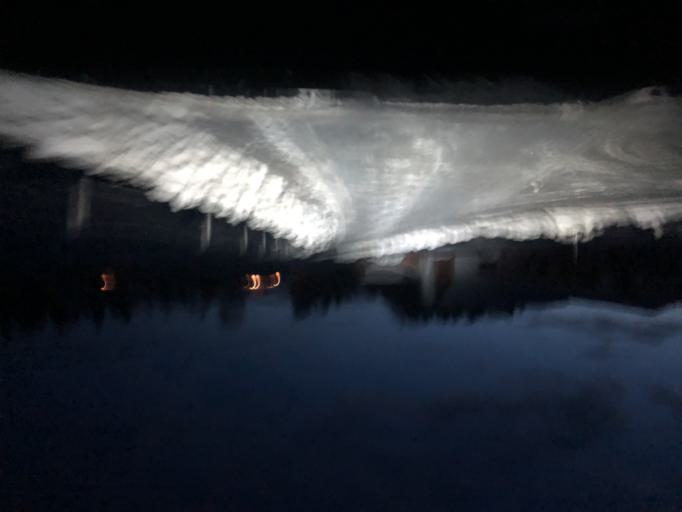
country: SE
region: Vaesternorrland
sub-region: Kramfors Kommun
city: Bollstabruk
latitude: 63.0548
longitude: 17.6496
